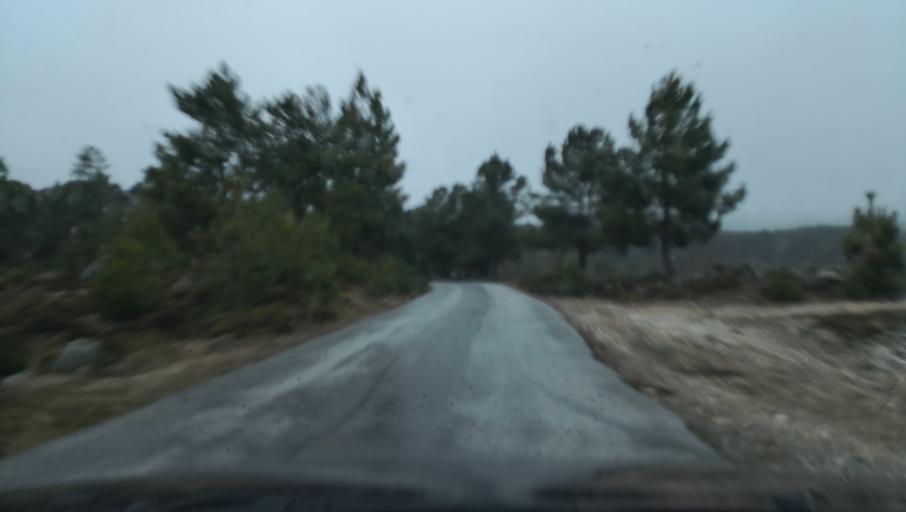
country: PT
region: Vila Real
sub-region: Vila Real
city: Vila Real
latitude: 41.3302
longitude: -7.7860
